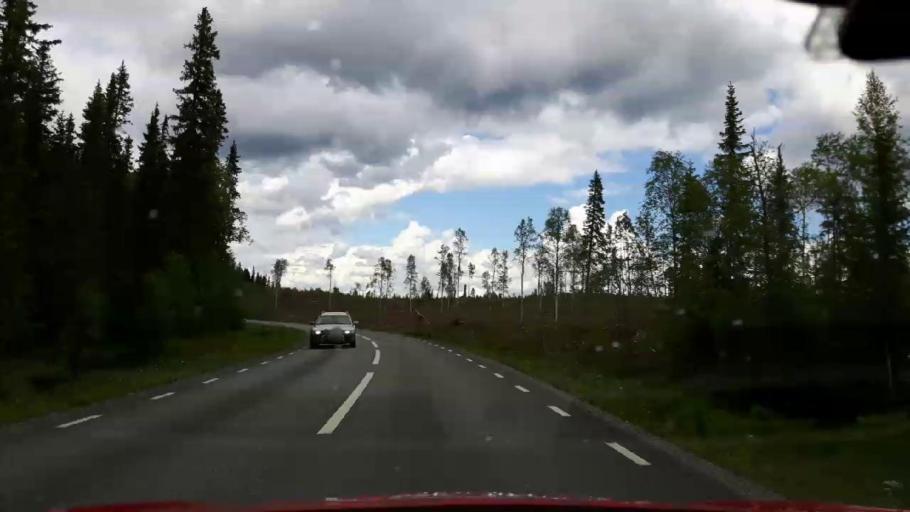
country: SE
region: Jaemtland
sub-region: Krokoms Kommun
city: Krokom
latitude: 63.7784
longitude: 14.3492
